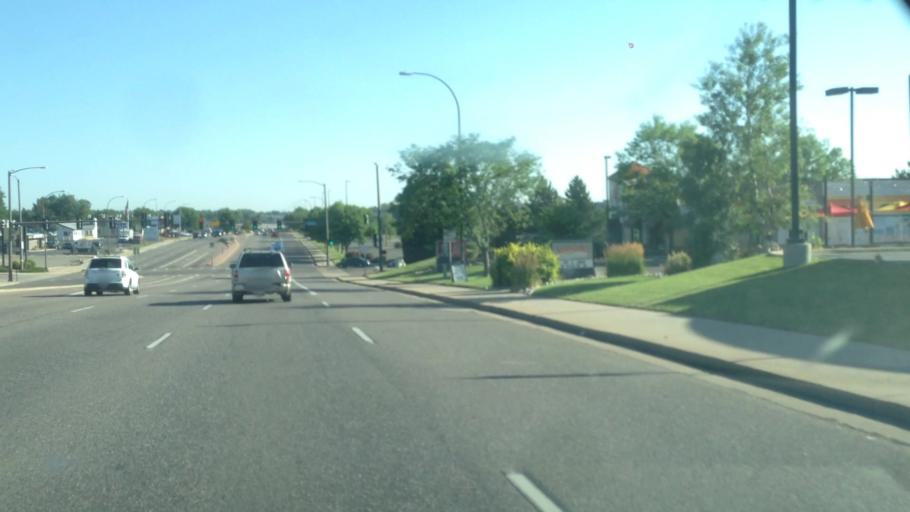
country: US
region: Colorado
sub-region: Jefferson County
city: Lakewood
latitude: 39.7191
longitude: -105.0814
